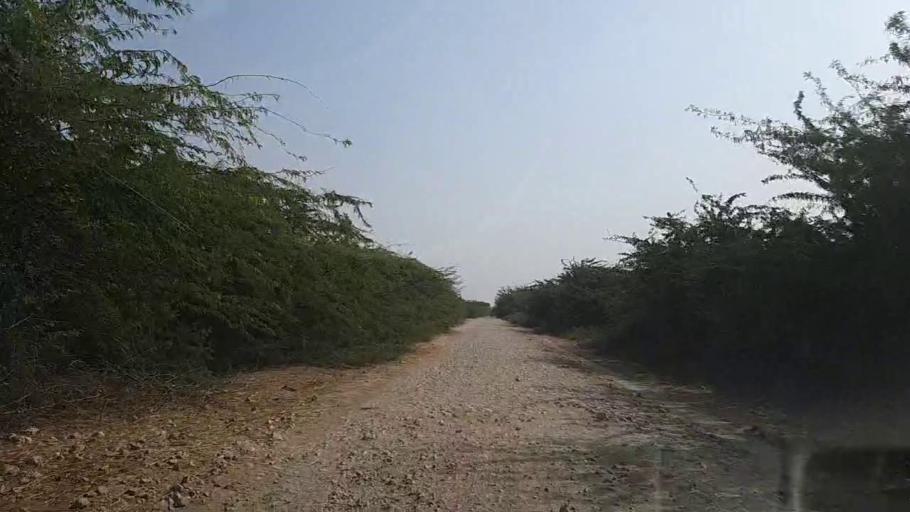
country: PK
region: Sindh
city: Keti Bandar
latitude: 24.2485
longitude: 67.6322
